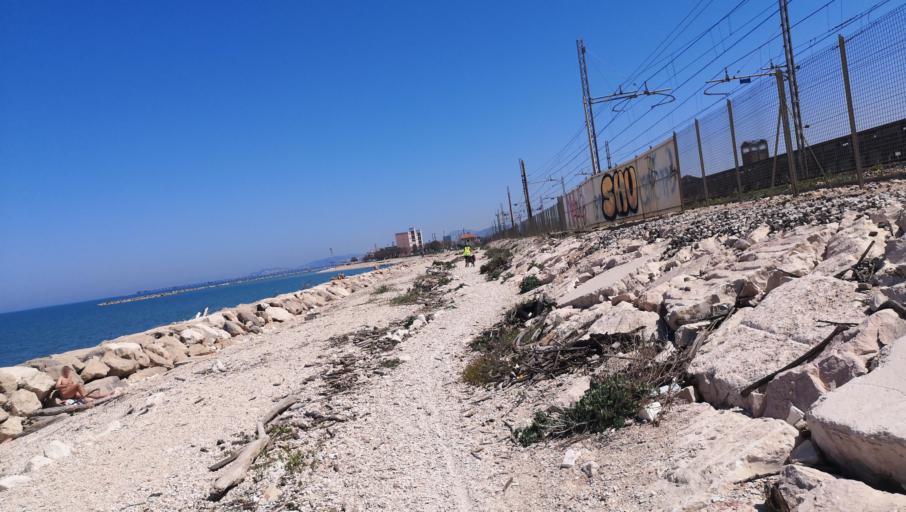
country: IT
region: The Marches
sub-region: Provincia di Ancona
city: Marina di Montemarciano
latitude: 43.6494
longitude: 13.3514
